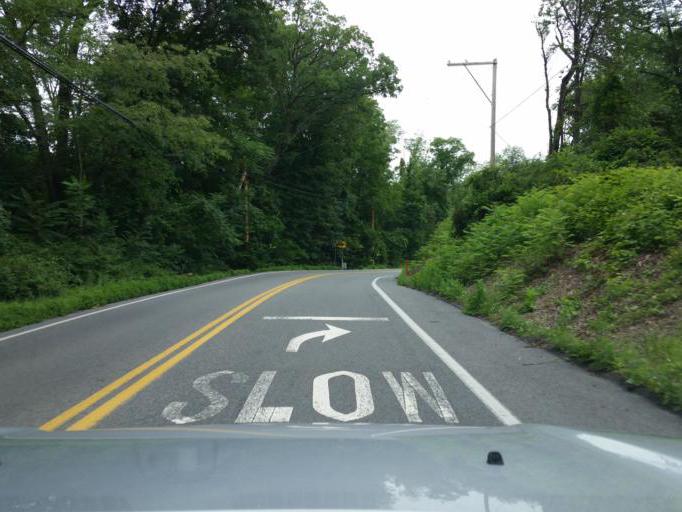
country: US
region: Pennsylvania
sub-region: Dauphin County
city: Rutherford
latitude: 40.2890
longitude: -76.7833
